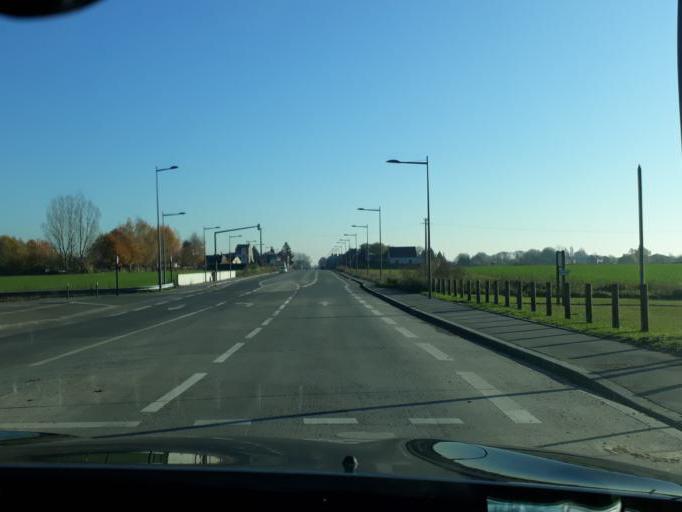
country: FR
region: Nord-Pas-de-Calais
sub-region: Departement du Nord
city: Lewarde
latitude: 50.3397
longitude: 3.1781
